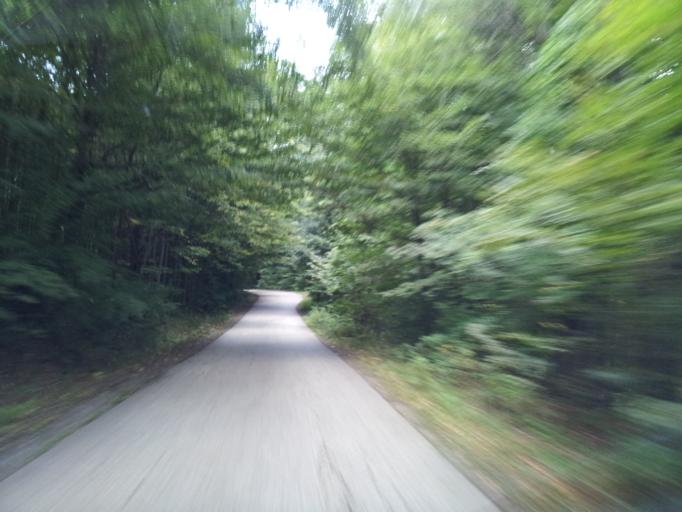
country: HU
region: Pest
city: Kismaros
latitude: 47.8856
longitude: 18.9661
